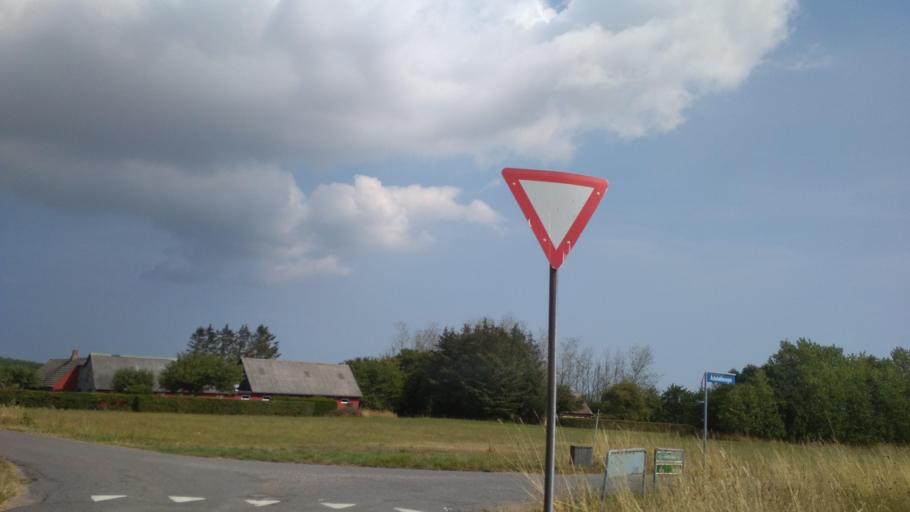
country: DK
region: Capital Region
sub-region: Bornholm Kommune
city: Akirkeby
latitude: 55.0558
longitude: 14.9454
